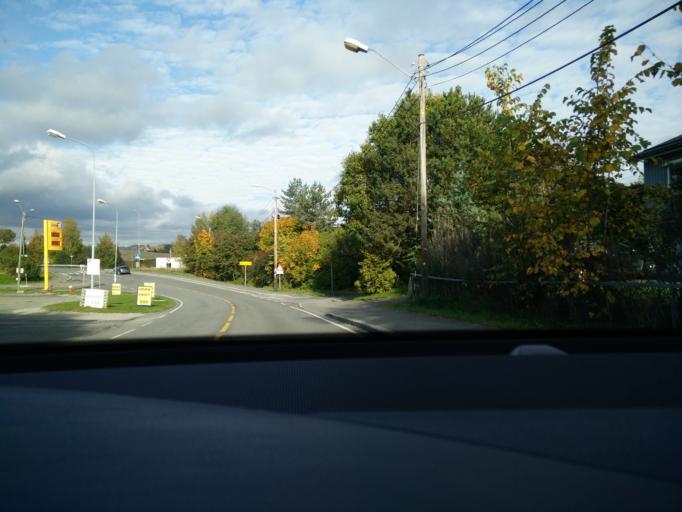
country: NO
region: Akershus
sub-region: Baerum
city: Lysaker
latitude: 59.9494
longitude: 10.6291
